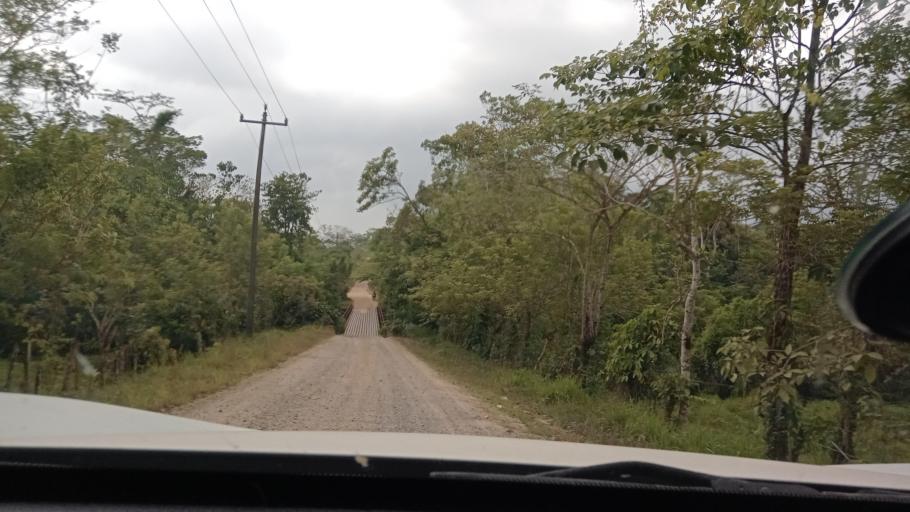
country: MX
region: Tabasco
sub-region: Huimanguillo
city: Francisco Rueda
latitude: 17.4322
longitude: -94.0446
